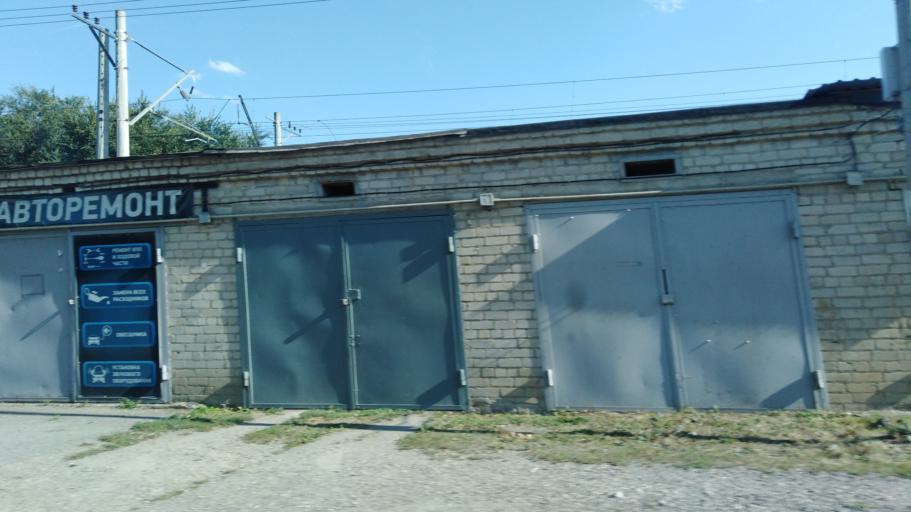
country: RU
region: Stavropol'skiy
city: Pyatigorsk
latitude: 44.0394
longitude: 43.0610
